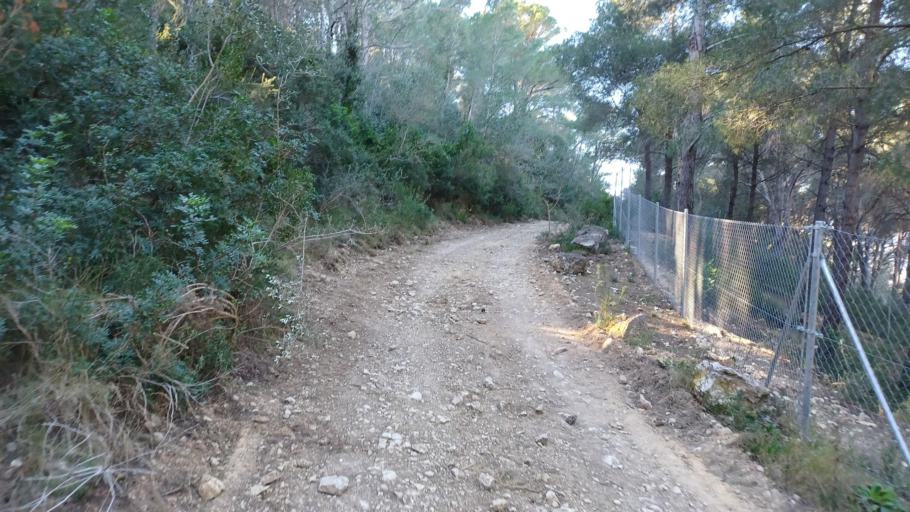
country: ES
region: Catalonia
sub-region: Provincia de Tarragona
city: Tortosa
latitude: 40.8106
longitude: 0.5681
